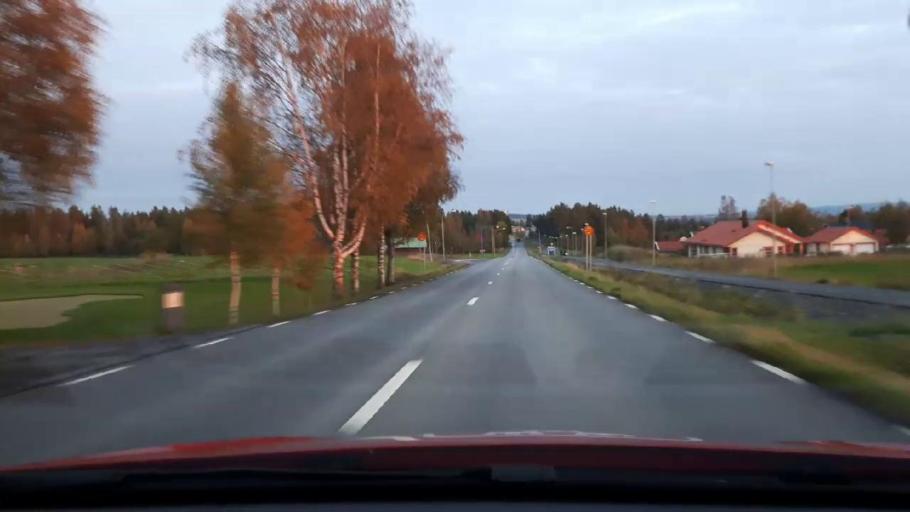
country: SE
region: Jaemtland
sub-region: OEstersunds Kommun
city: Ostersund
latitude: 63.2231
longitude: 14.6000
